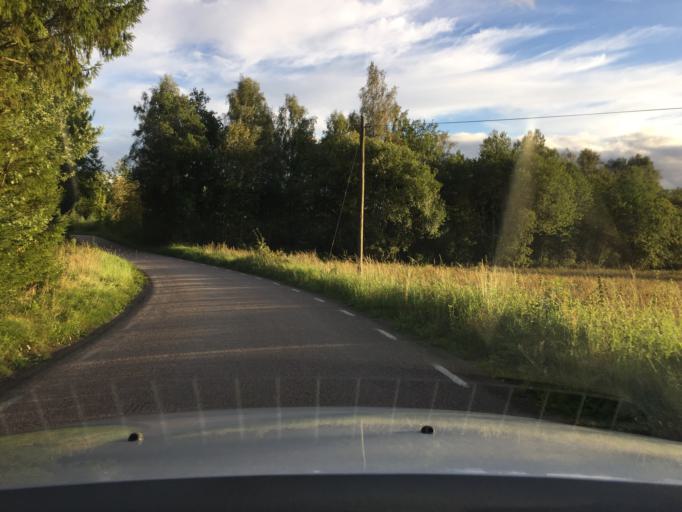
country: SE
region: Skane
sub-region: Hassleholms Kommun
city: Tormestorp
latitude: 56.0176
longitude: 13.7747
